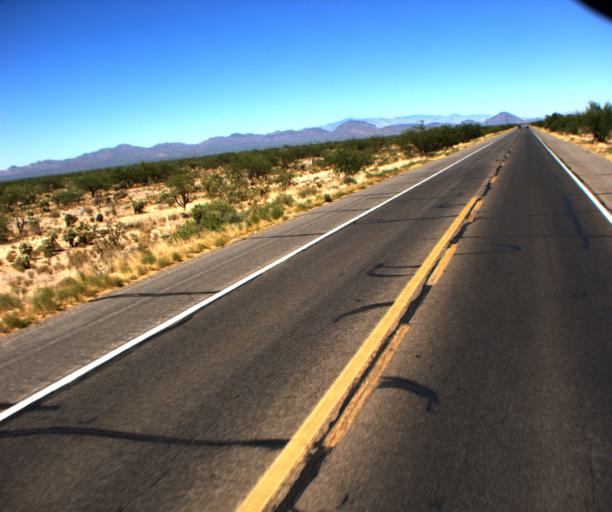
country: US
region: Arizona
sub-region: Pima County
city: Three Points
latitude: 32.0984
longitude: -111.2589
